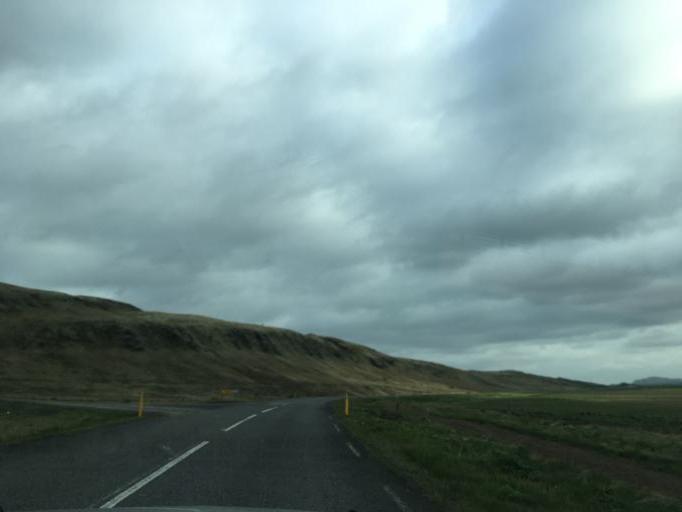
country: IS
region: South
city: Vestmannaeyjar
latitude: 64.1729
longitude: -20.2847
